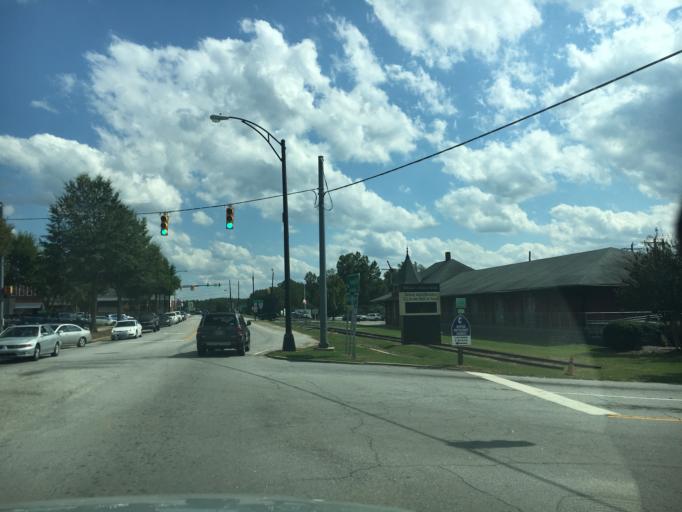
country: US
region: South Carolina
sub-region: Anderson County
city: Belton
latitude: 34.5230
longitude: -82.4942
